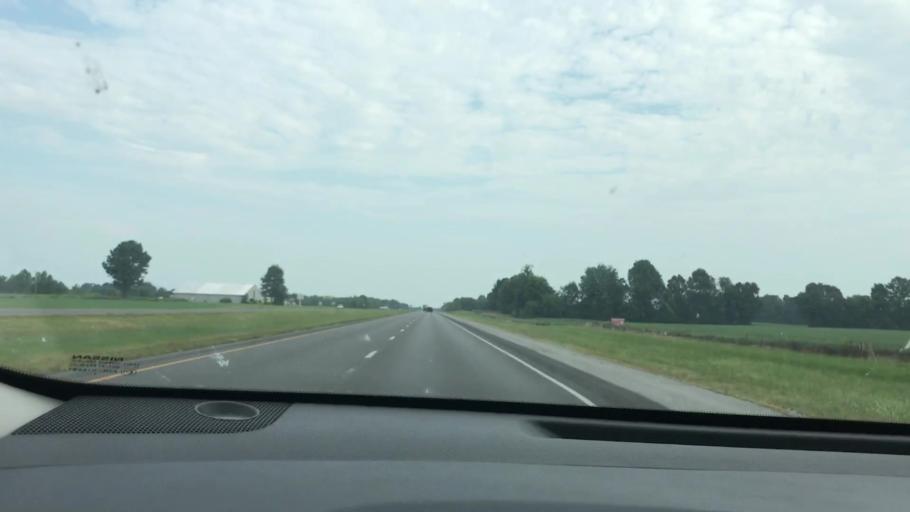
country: US
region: Kentucky
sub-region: Calloway County
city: Murray
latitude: 36.6876
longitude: -88.3029
